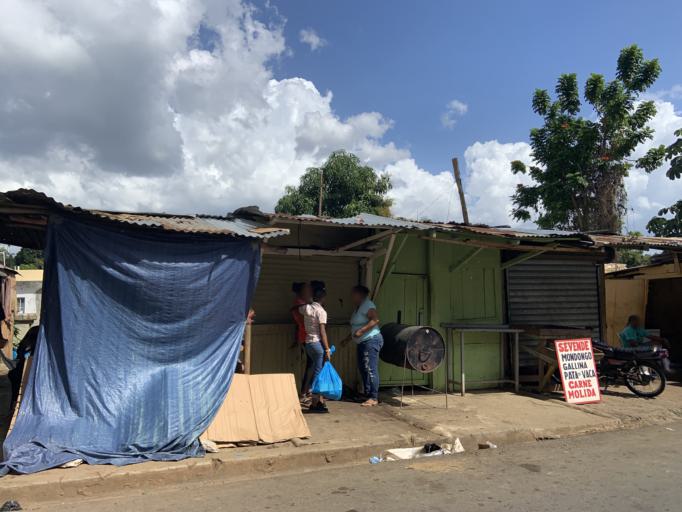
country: DO
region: Monte Plata
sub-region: Yamasa
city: Yamasa
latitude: 18.7737
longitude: -70.0259
